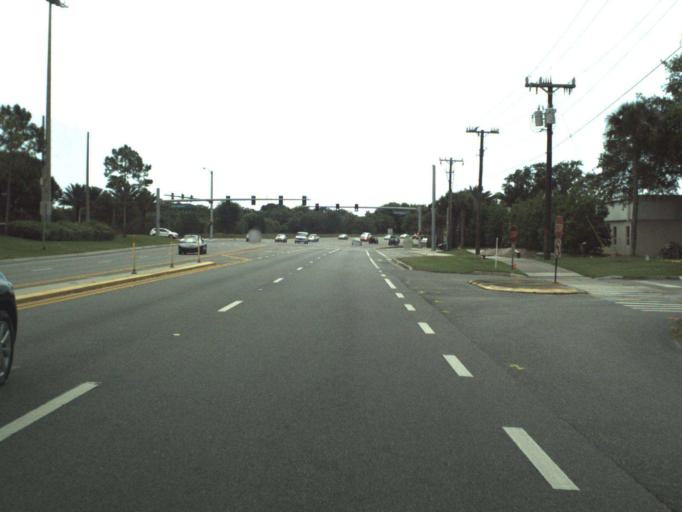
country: US
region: Florida
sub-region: Volusia County
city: Daytona Beach
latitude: 29.1893
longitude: -81.0457
